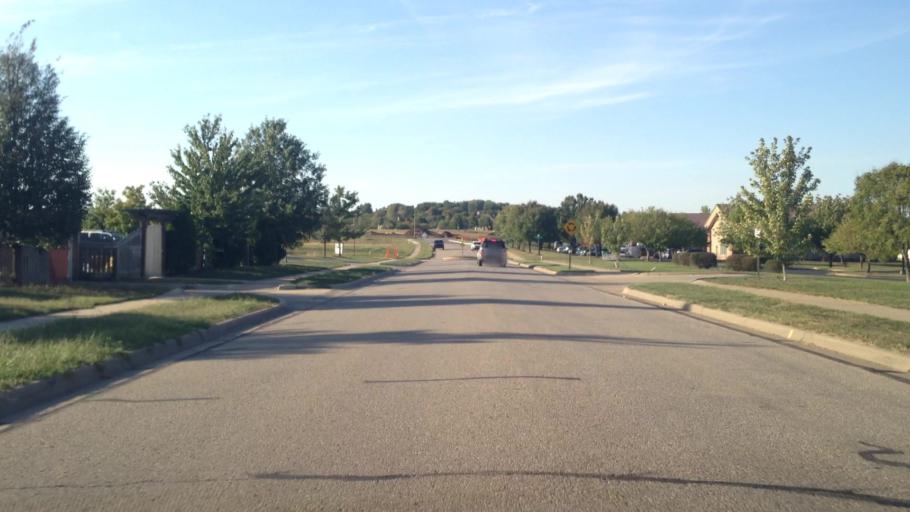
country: US
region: Kansas
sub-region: Douglas County
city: Lawrence
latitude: 38.9616
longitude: -95.3101
